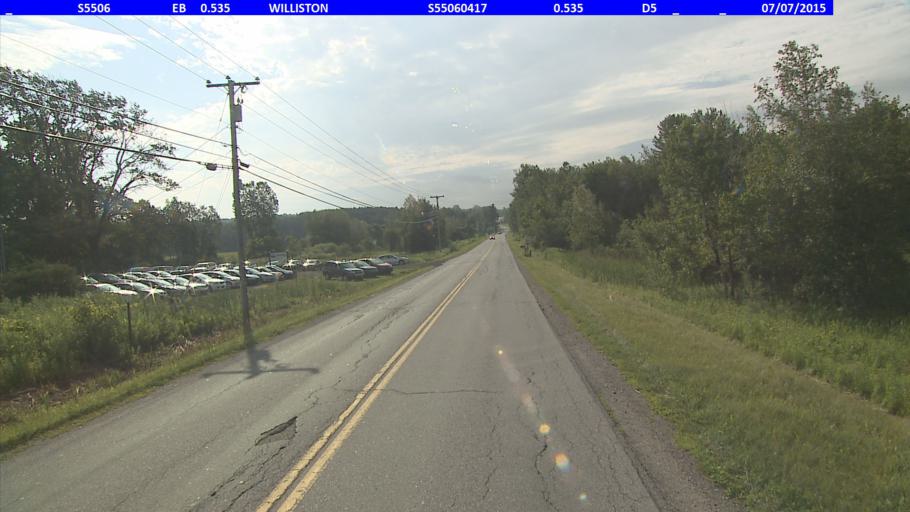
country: US
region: Vermont
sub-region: Chittenden County
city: Essex Junction
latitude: 44.4651
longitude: -73.1025
